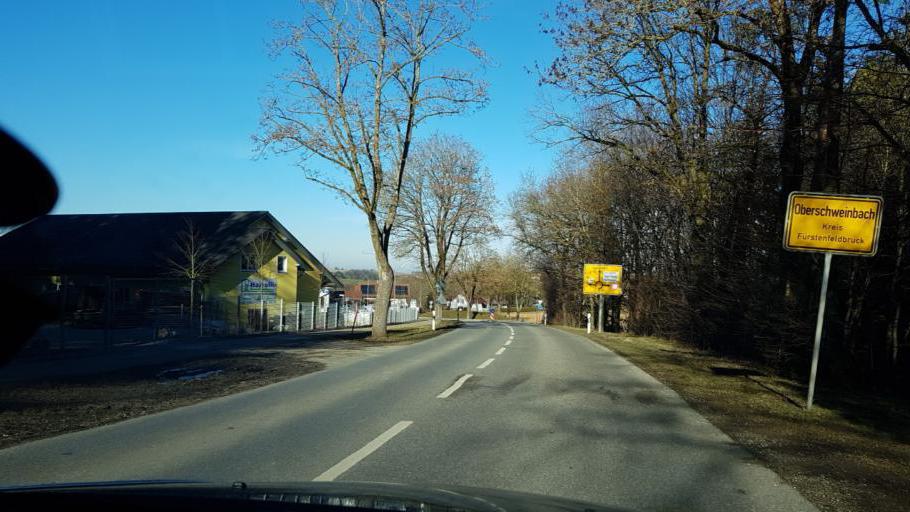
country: DE
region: Bavaria
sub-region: Upper Bavaria
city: Oberschweinbach
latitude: 48.2335
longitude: 11.1657
